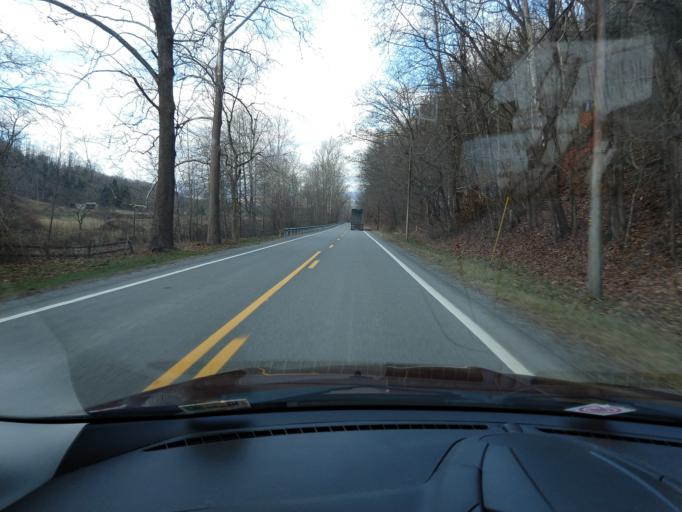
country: US
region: West Virginia
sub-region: Randolph County
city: Elkins
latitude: 38.6760
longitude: -79.9553
